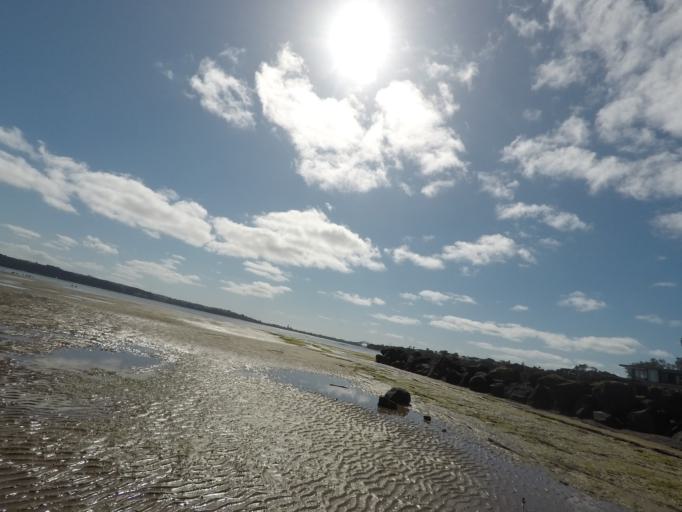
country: NZ
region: Auckland
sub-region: Auckland
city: Rosebank
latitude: -36.8522
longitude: 174.7139
